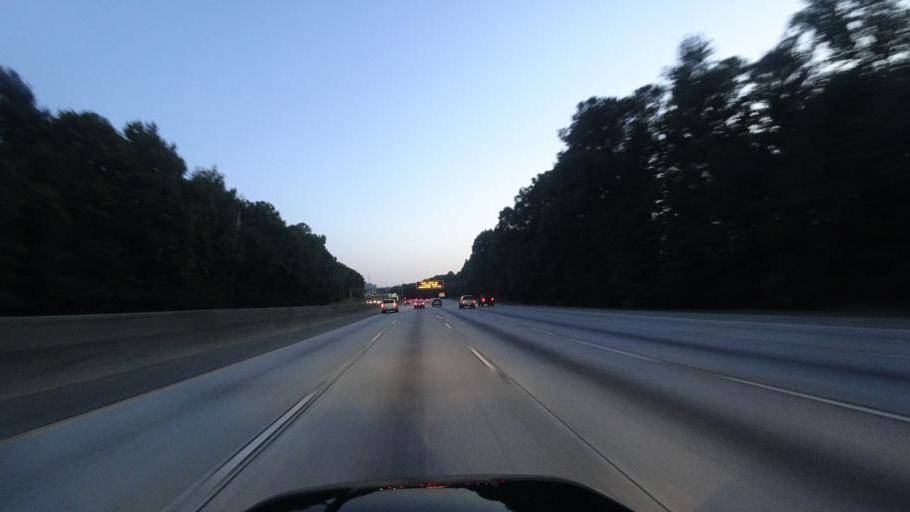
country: US
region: Georgia
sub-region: DeKalb County
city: Clarkston
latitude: 33.8350
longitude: -84.2499
